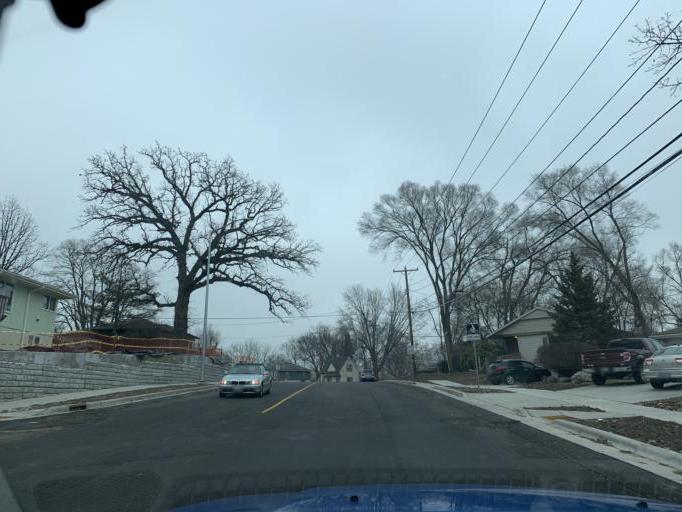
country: US
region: Wisconsin
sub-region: Dane County
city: Monona
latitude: 43.0745
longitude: -89.3169
